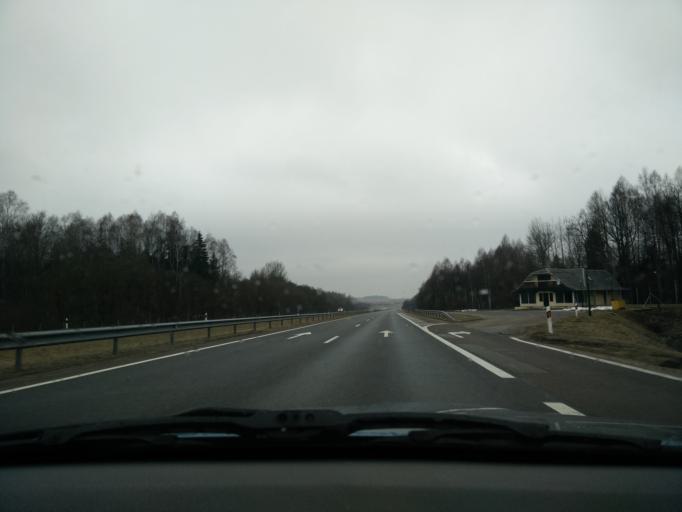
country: LT
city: Silale
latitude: 55.5736
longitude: 22.1683
